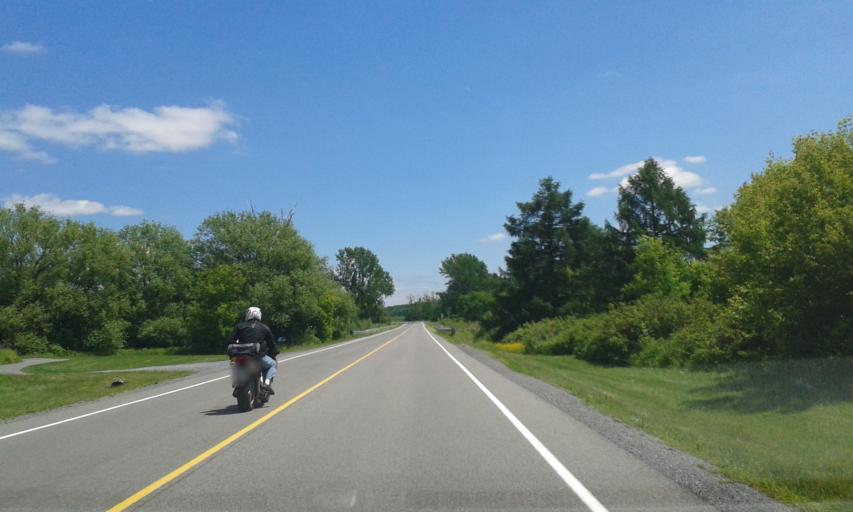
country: US
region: New York
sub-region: St. Lawrence County
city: Massena
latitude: 44.9970
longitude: -74.9106
